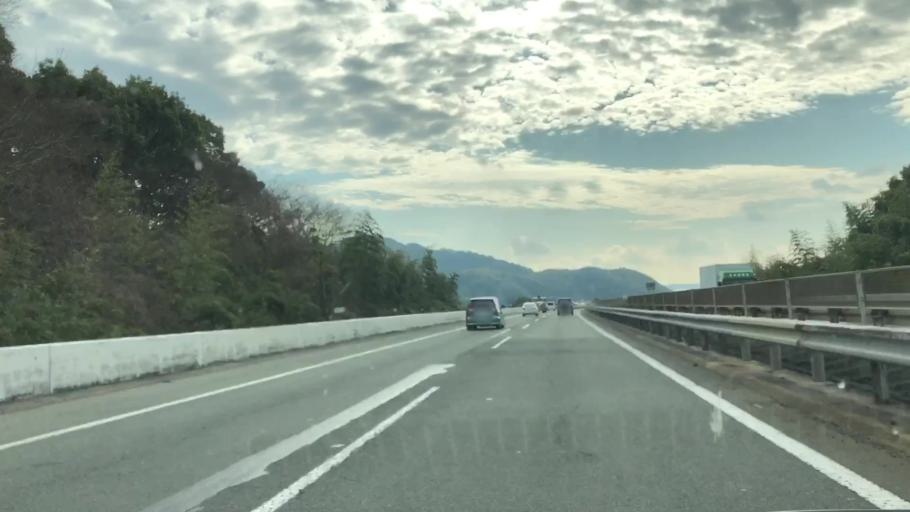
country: JP
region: Fukuoka
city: Setakamachi-takayanagi
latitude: 33.1816
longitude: 130.5182
